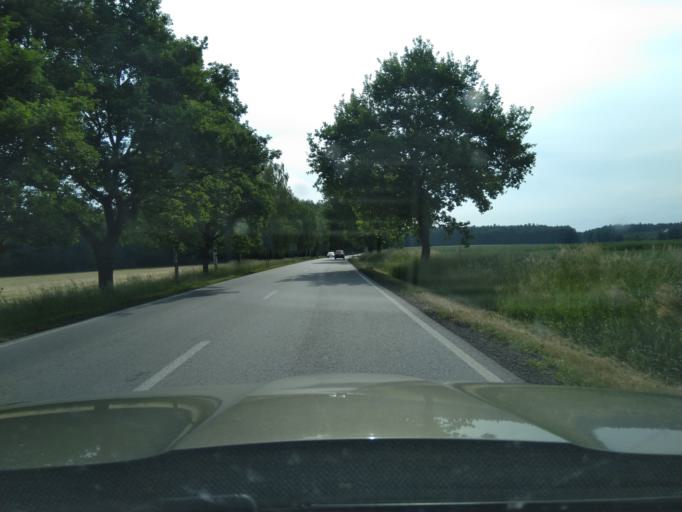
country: CZ
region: Jihocesky
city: Zliv
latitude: 49.0310
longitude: 14.3035
